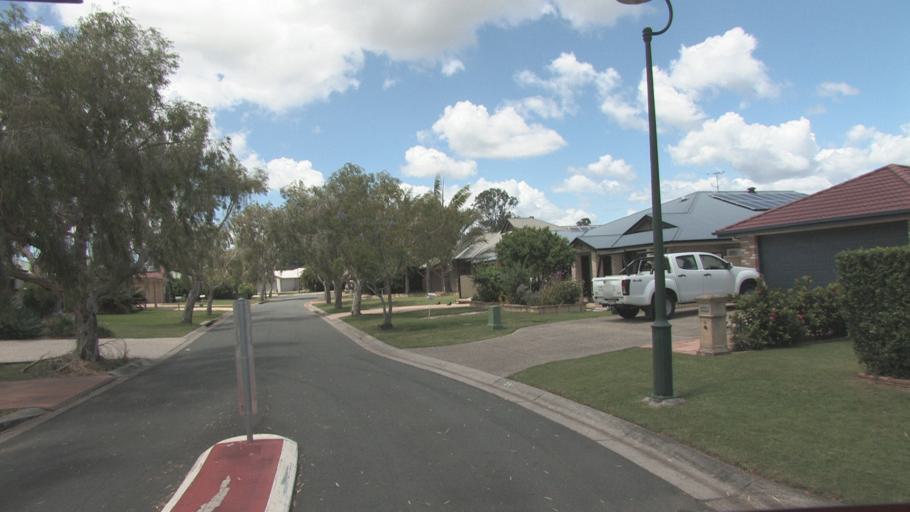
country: AU
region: Queensland
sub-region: Logan
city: Beenleigh
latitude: -27.6867
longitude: 153.1757
